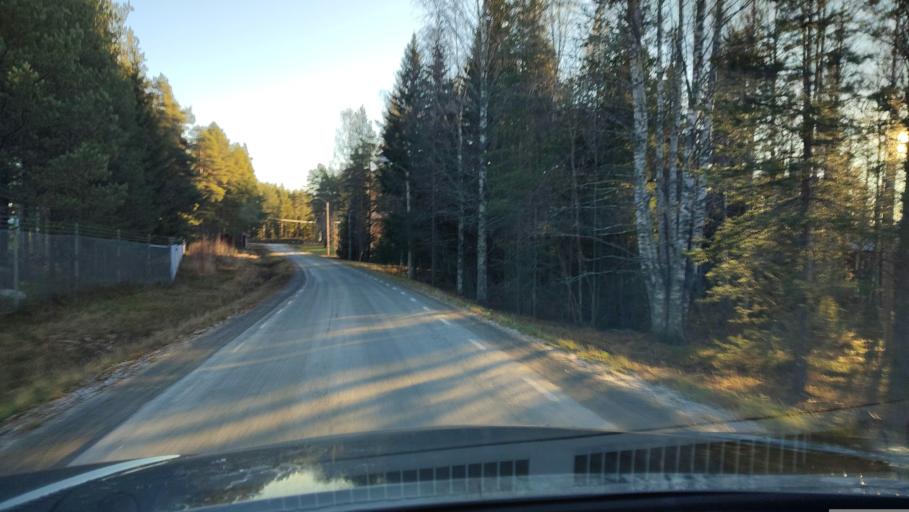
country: SE
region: Vaesterbotten
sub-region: Skelleftea Kommun
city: Viken
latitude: 64.7012
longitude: 20.9049
